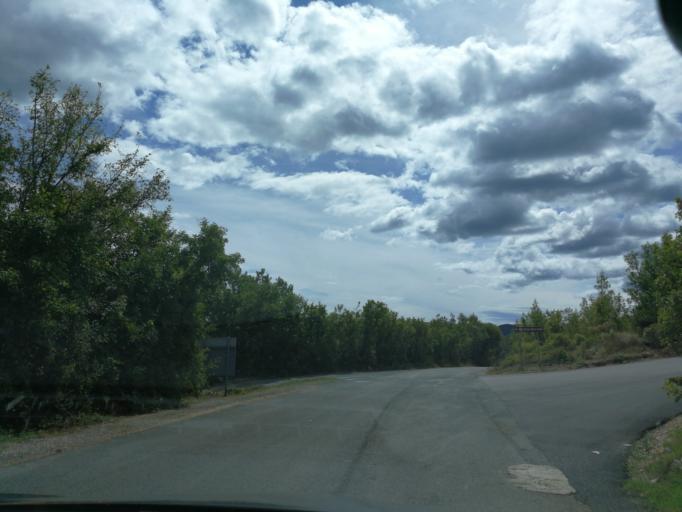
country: HR
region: Primorsko-Goranska
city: Njivice
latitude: 45.1635
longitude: 14.6022
